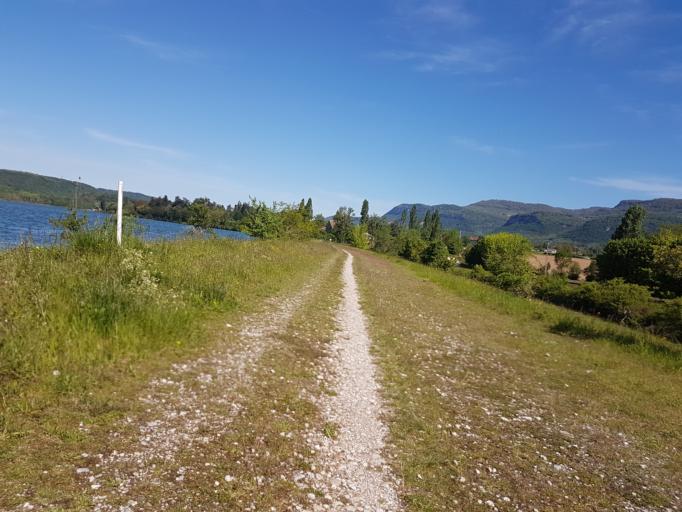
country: FR
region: Rhone-Alpes
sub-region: Departement de l'Ain
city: Villebois
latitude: 45.8341
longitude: 5.4342
